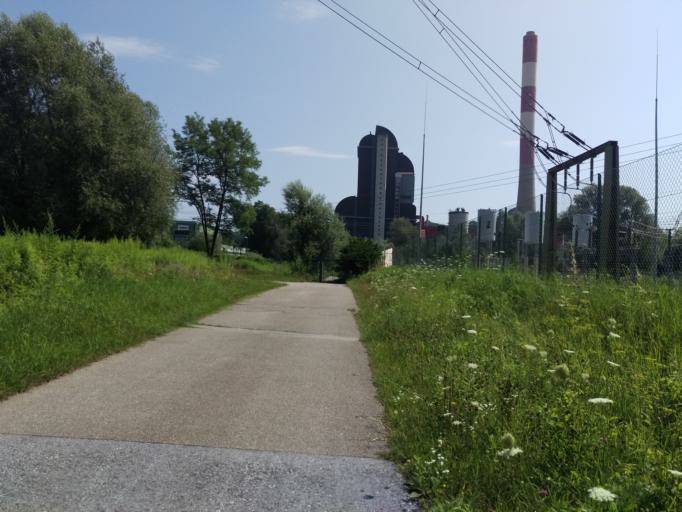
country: AT
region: Styria
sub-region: Politischer Bezirk Graz-Umgebung
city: Werndorf
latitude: 46.9099
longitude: 15.4834
